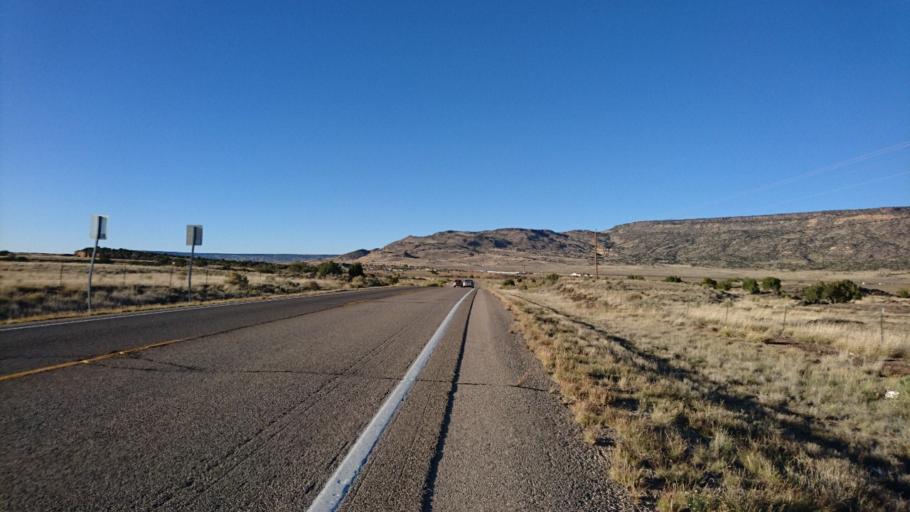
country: US
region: New Mexico
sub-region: Cibola County
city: Grants
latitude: 35.0917
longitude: -107.7709
